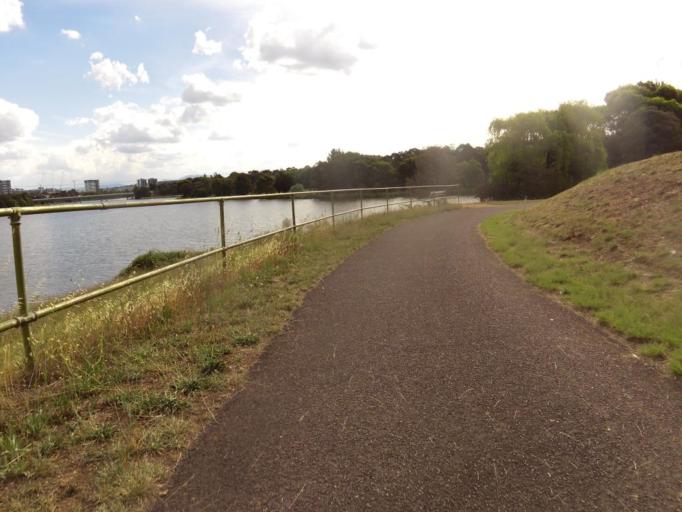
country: AU
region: Australian Capital Territory
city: Belconnen
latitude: -35.2233
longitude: 149.0809
